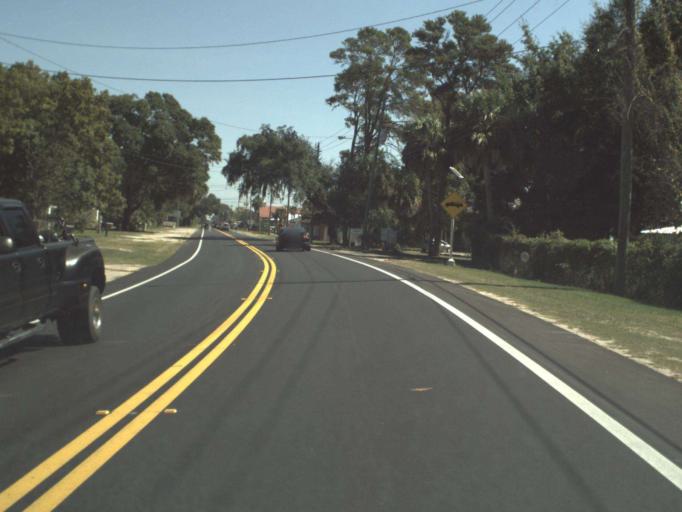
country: US
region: Florida
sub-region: Bay County
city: Parker
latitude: 30.1311
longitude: -85.6119
